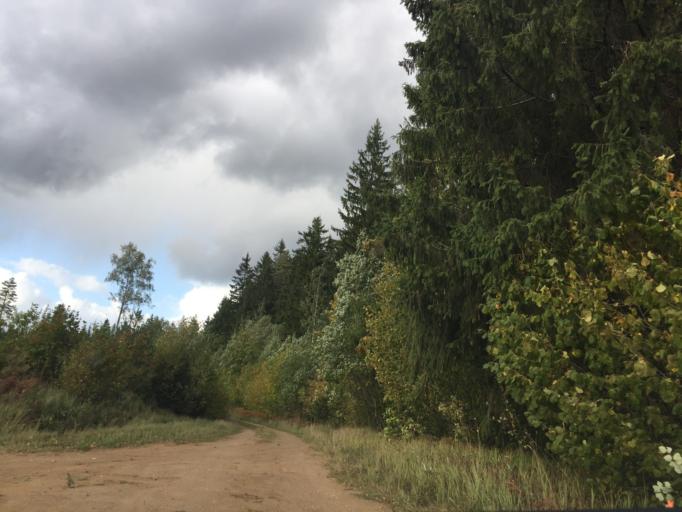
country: LV
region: Ligatne
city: Ligatne
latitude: 57.1012
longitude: 25.1495
